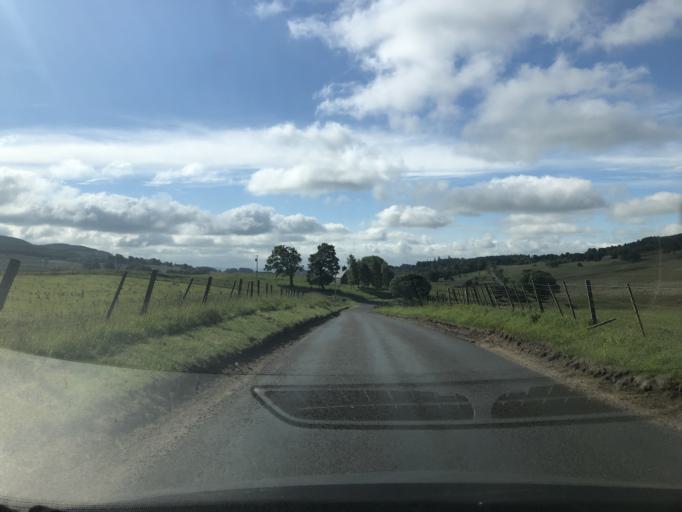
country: GB
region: Scotland
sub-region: Angus
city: Kirriemuir
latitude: 56.7576
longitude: -3.0170
